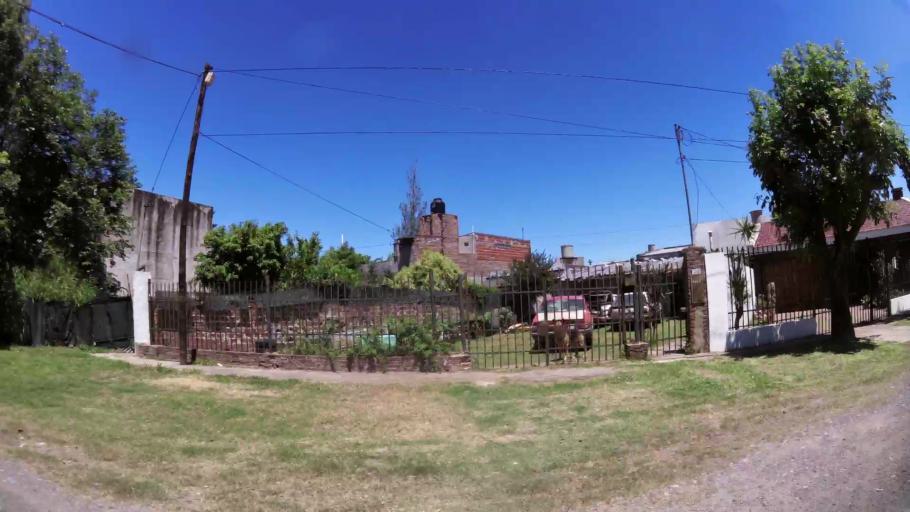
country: AR
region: Santa Fe
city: Santa Fe de la Vera Cruz
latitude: -31.6260
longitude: -60.7081
